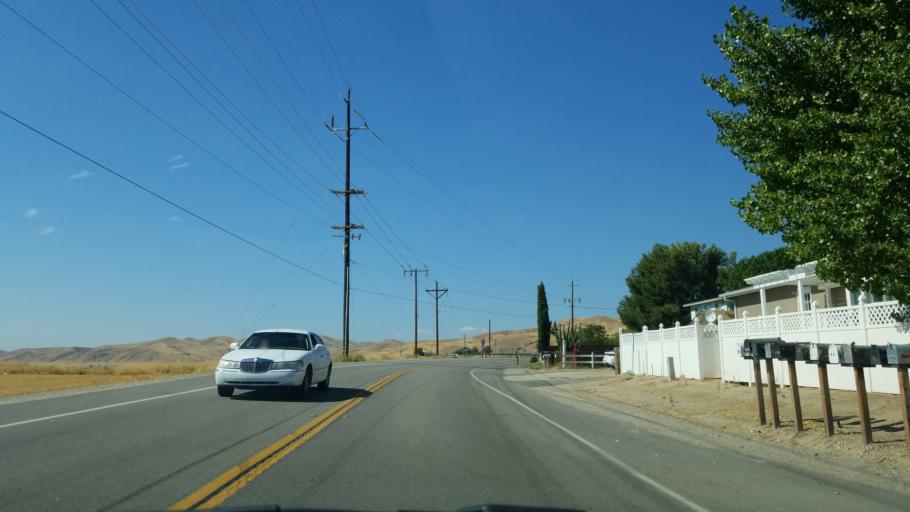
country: US
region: California
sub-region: San Luis Obispo County
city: San Miguel
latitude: 35.7449
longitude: -120.6851
